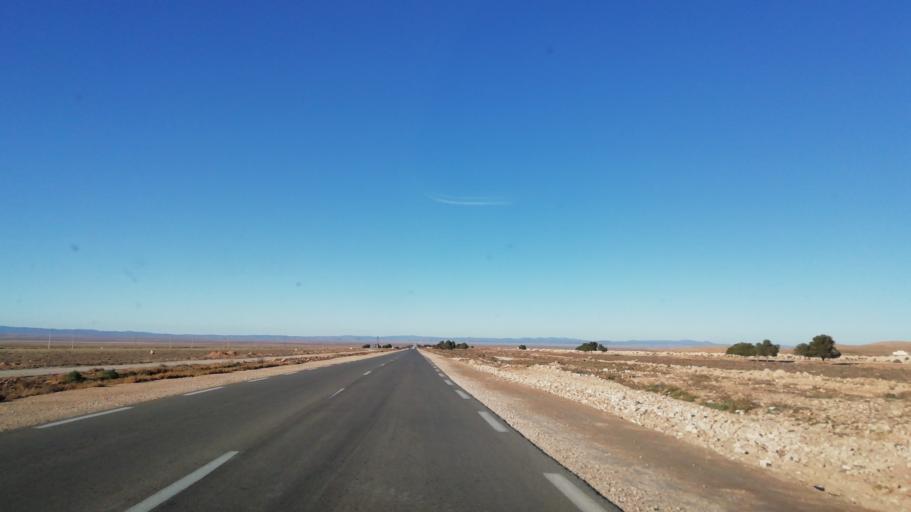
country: DZ
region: Tlemcen
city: Sebdou
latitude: 34.3013
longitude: -1.2612
